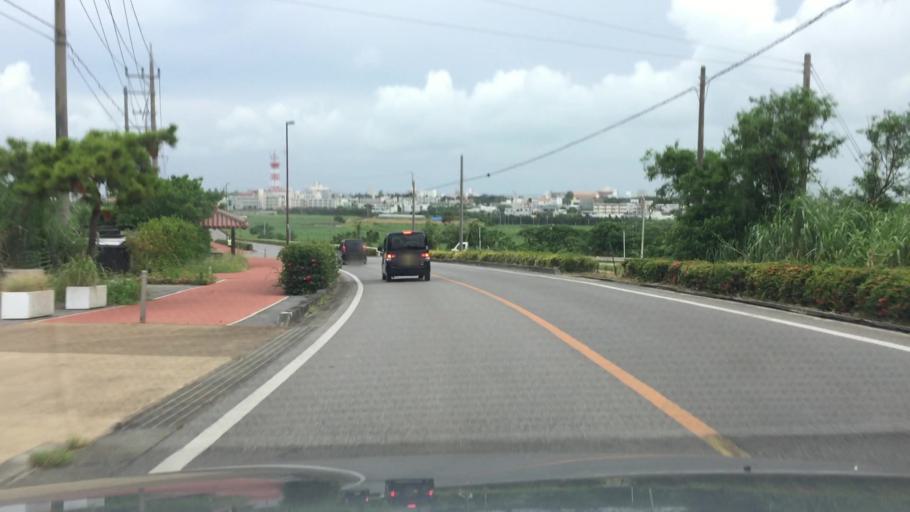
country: JP
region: Okinawa
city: Ishigaki
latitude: 24.3588
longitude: 124.1569
